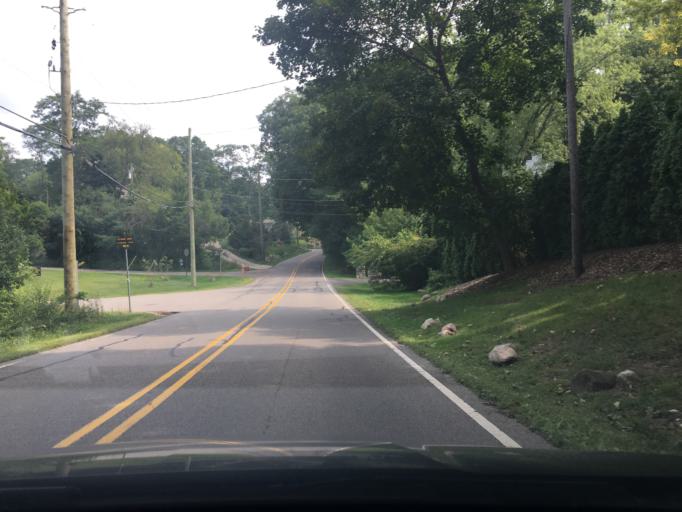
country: US
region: Michigan
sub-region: Oakland County
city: Bloomfield Hills
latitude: 42.5836
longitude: -83.2312
